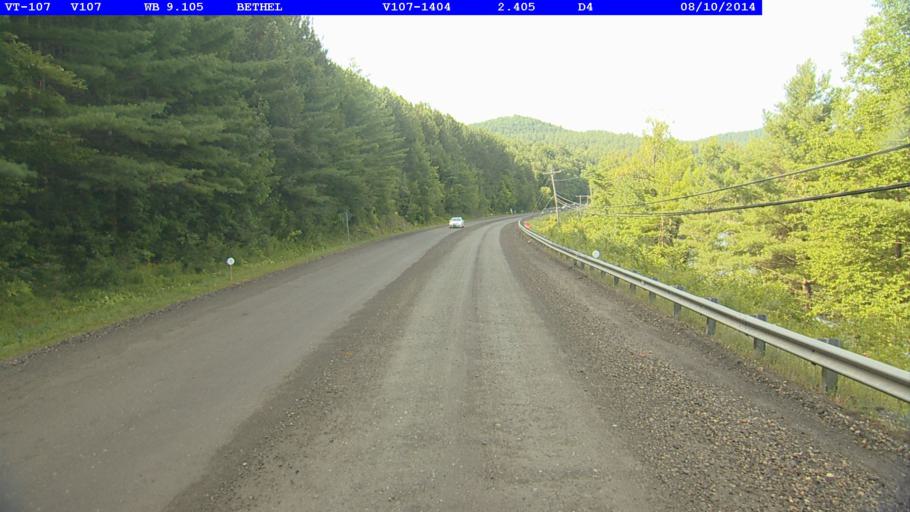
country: US
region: Vermont
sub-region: Orange County
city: Randolph
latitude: 43.8155
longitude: -72.6364
